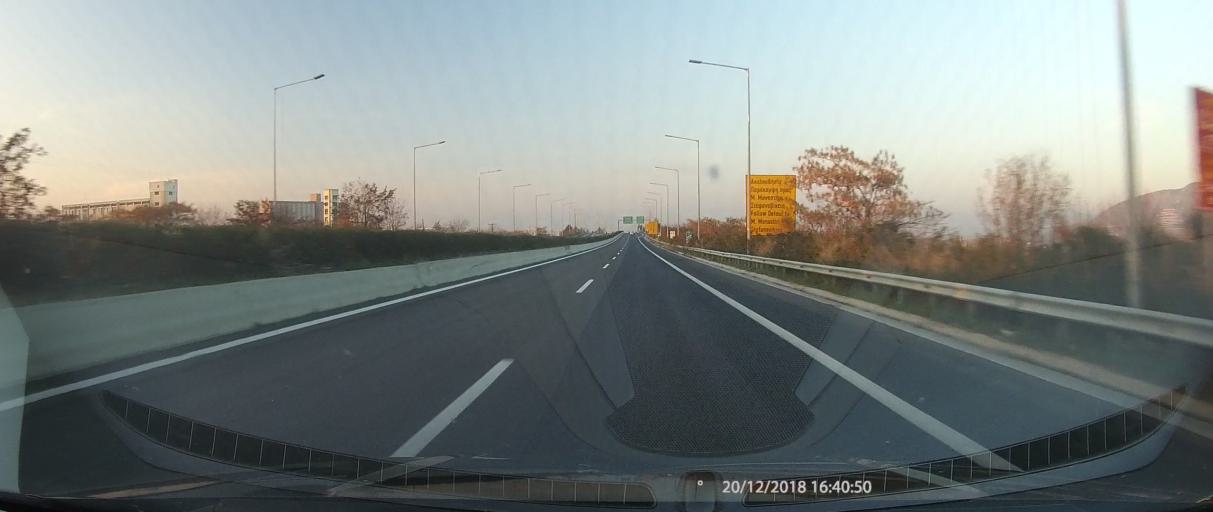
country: GR
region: Thessaly
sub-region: Nomos Magnisias
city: Velestino
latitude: 39.3819
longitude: 22.7681
